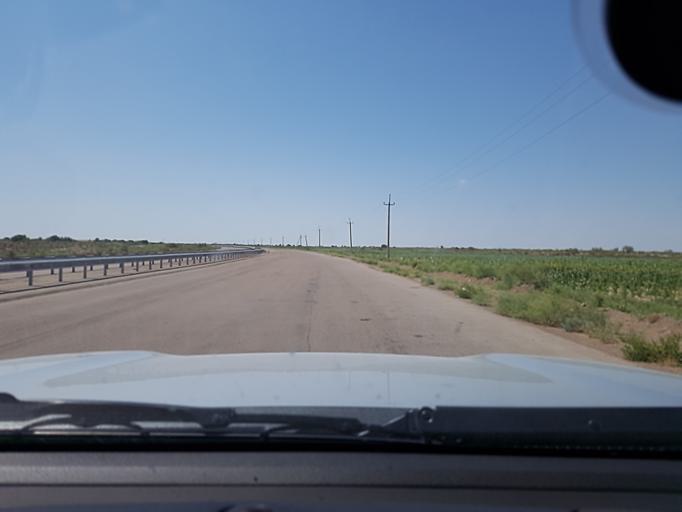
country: TM
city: Akdepe
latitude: 41.7494
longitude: 59.2608
